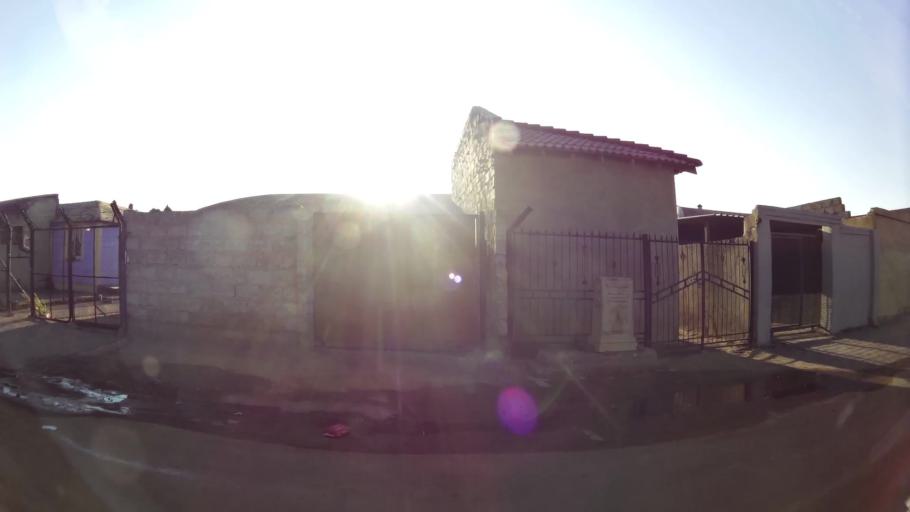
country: ZA
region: Gauteng
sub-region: City of Johannesburg Metropolitan Municipality
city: Soweto
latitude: -26.2544
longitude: 27.8822
